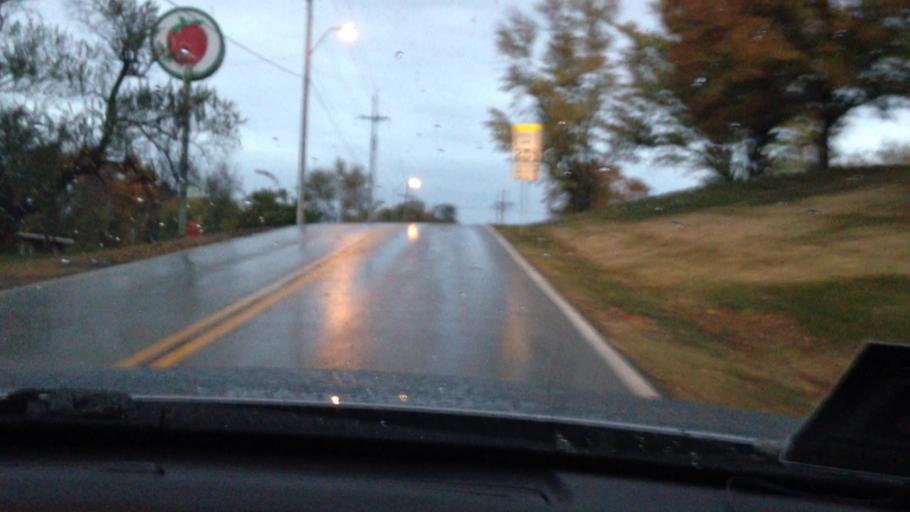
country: US
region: Missouri
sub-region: Platte County
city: Riverside
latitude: 39.2008
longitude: -94.6316
